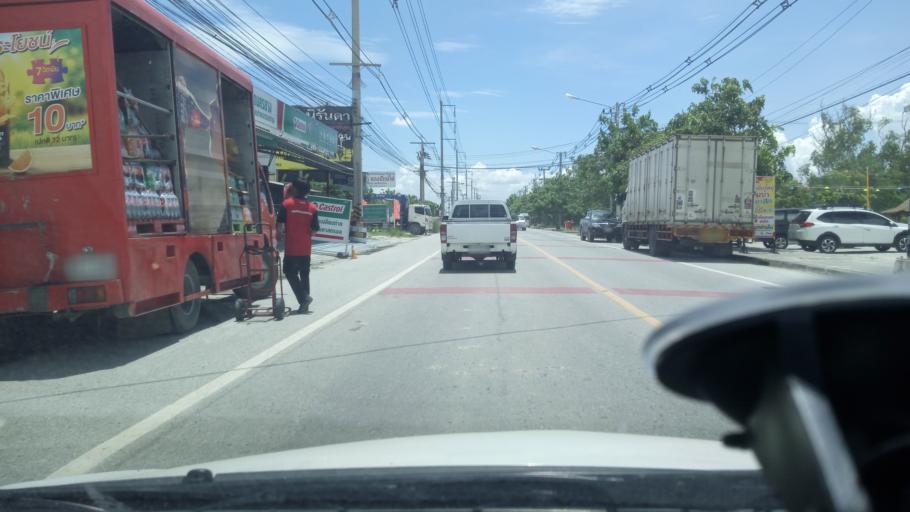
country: TH
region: Chon Buri
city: Phan Thong
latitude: 13.4430
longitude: 101.0593
